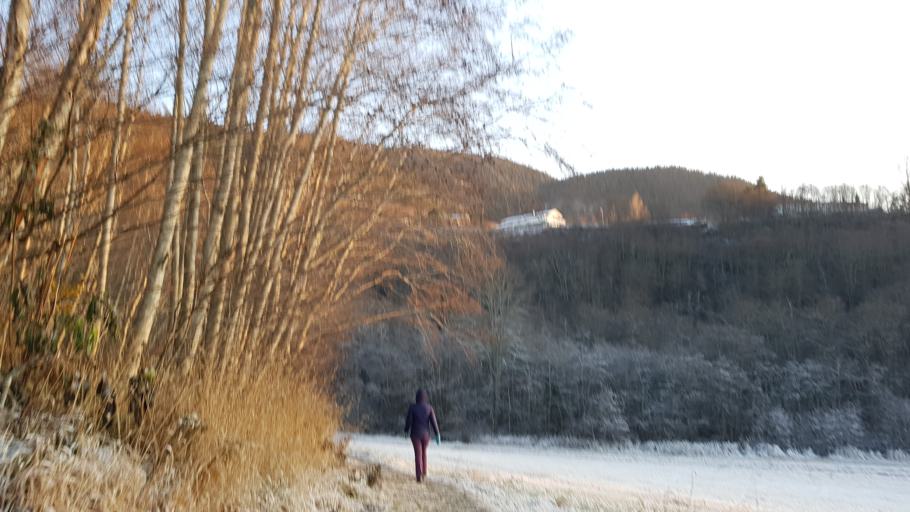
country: NO
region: Sor-Trondelag
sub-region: Melhus
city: Melhus
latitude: 63.2749
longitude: 10.2977
